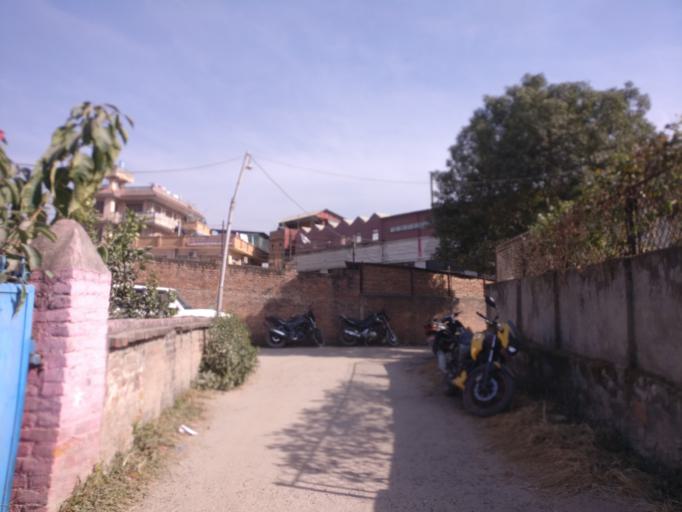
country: NP
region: Central Region
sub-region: Bagmati Zone
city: Patan
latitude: 27.6708
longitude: 85.3379
